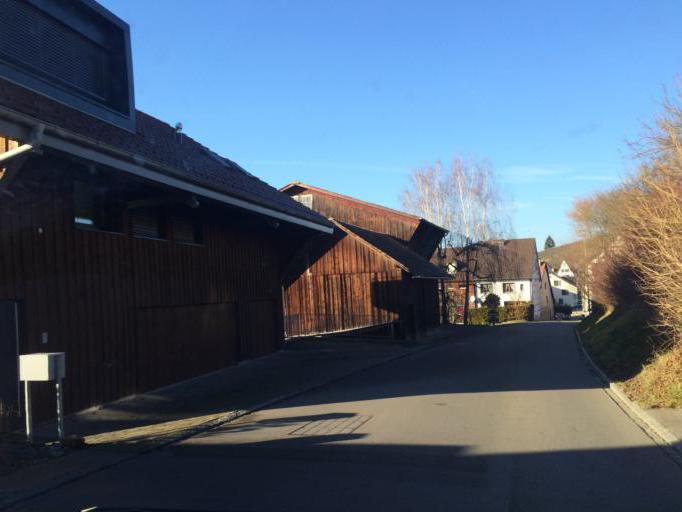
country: CH
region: Thurgau
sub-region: Frauenfeld District
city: Diessenhofen
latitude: 47.7037
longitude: 8.7254
